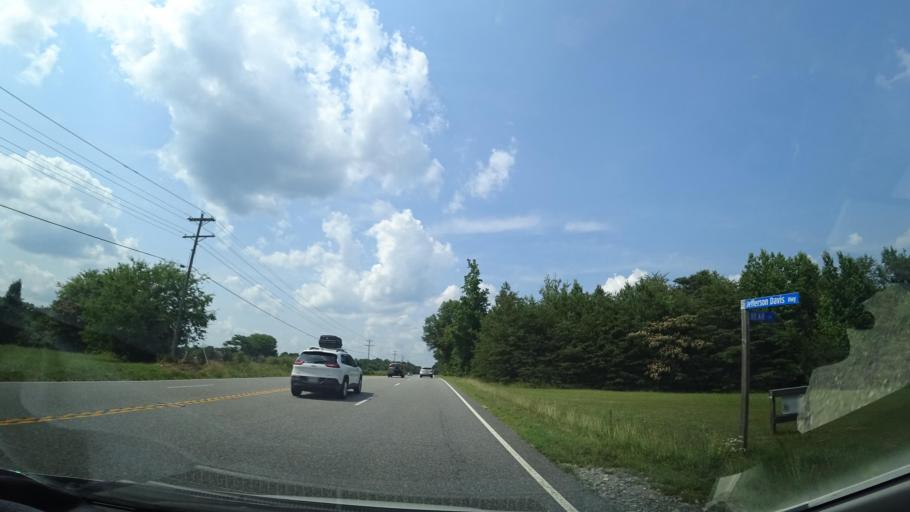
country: US
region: Virginia
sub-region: Hanover County
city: Ashland
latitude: 37.9222
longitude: -77.4777
